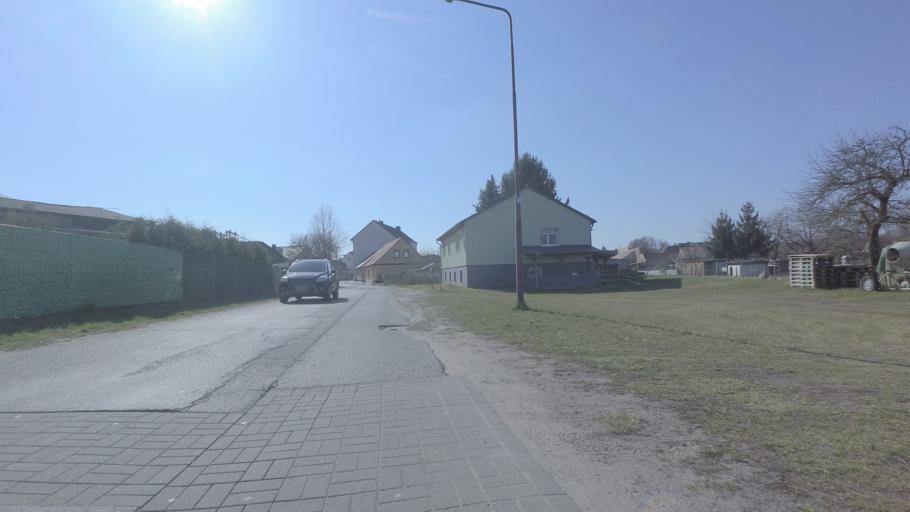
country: DE
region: Brandenburg
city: Halbe
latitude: 52.1094
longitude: 13.7679
